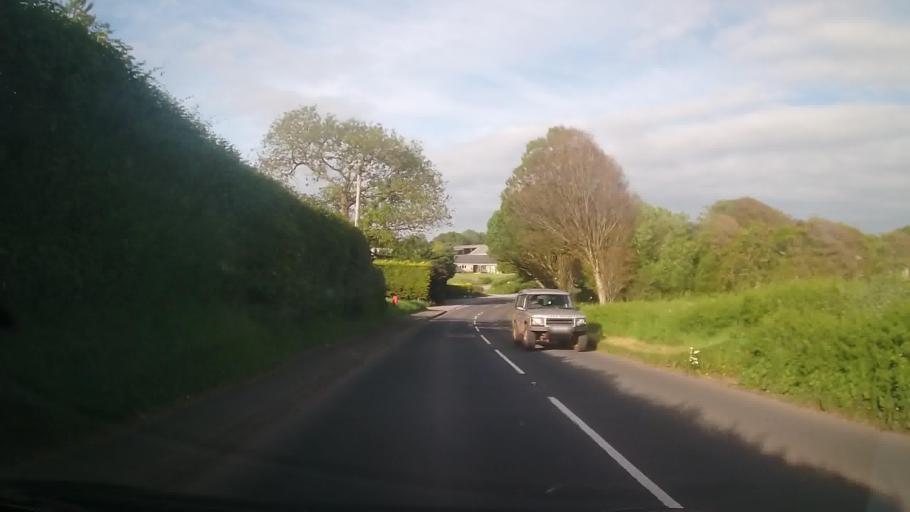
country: GB
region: England
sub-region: Devon
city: Modbury
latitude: 50.3493
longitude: -3.8969
